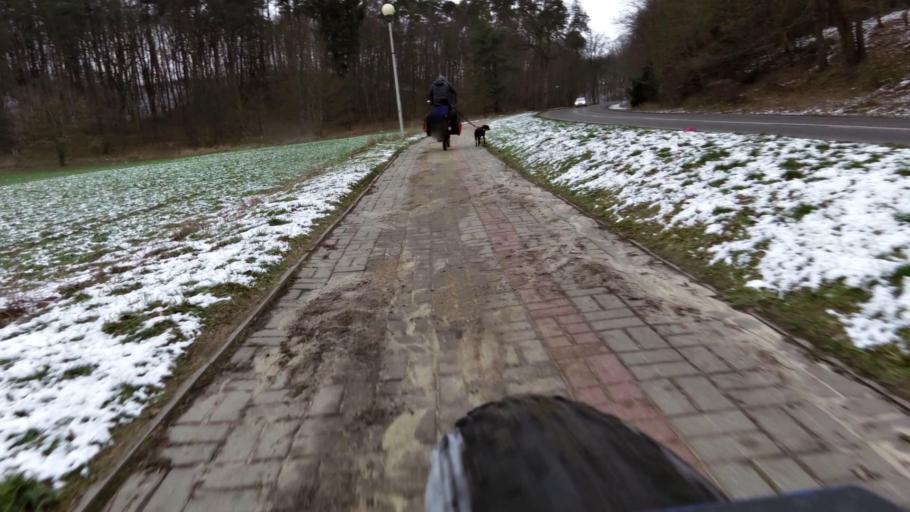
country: PL
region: West Pomeranian Voivodeship
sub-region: Powiat walecki
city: Miroslawiec
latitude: 53.3562
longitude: 16.0851
